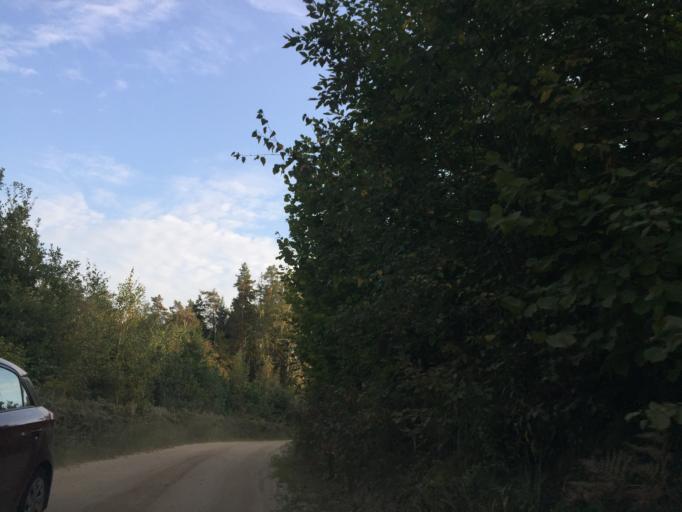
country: LV
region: Baldone
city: Baldone
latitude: 56.7634
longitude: 24.4088
